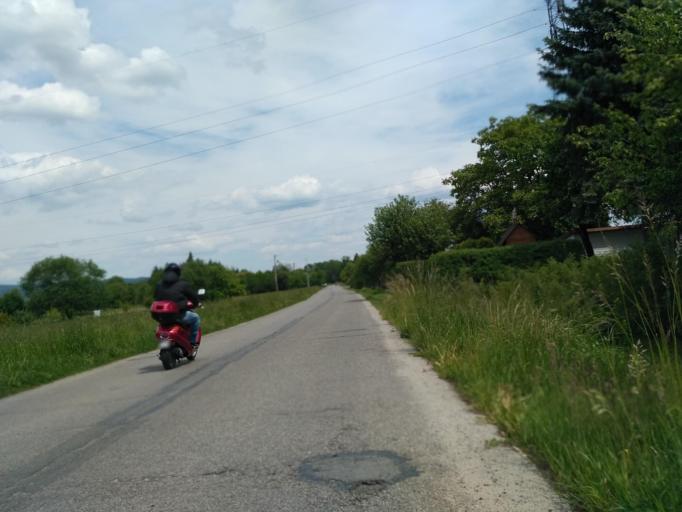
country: PL
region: Subcarpathian Voivodeship
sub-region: Powiat krosnienski
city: Odrzykon
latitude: 49.7098
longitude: 21.7324
